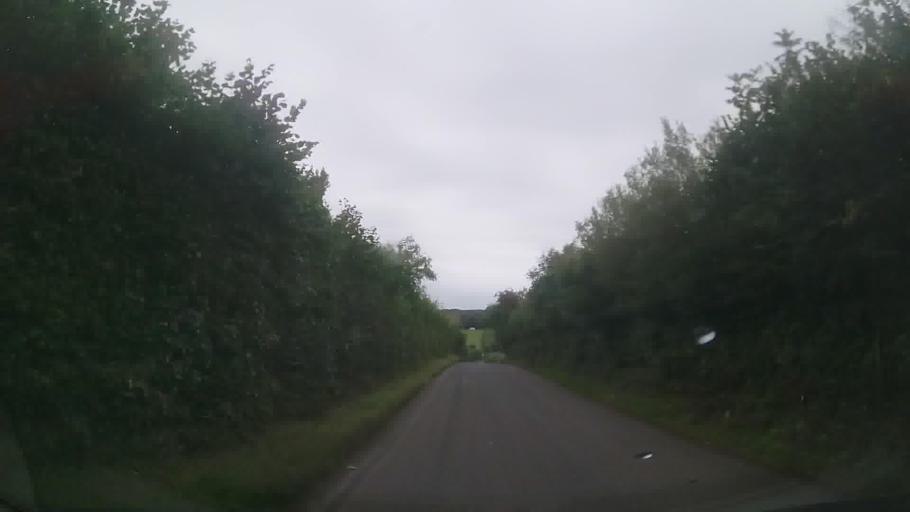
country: GB
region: Wales
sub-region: Pembrokeshire
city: Saundersfoot
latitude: 51.7369
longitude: -4.6370
